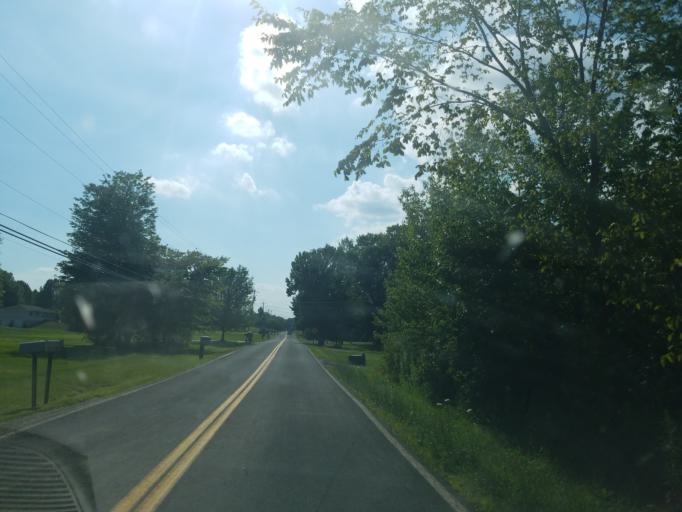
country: US
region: Ohio
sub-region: Portage County
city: Brimfield
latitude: 41.0504
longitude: -81.3167
